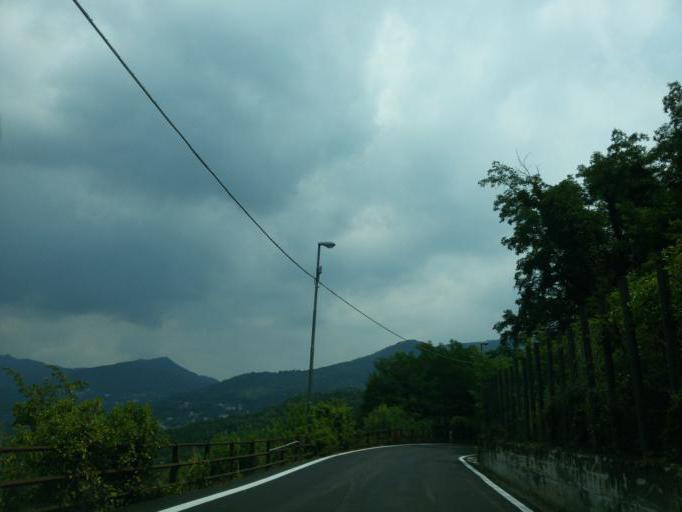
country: IT
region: Liguria
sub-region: Provincia di Genova
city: Piccarello
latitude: 44.4418
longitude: 9.0023
